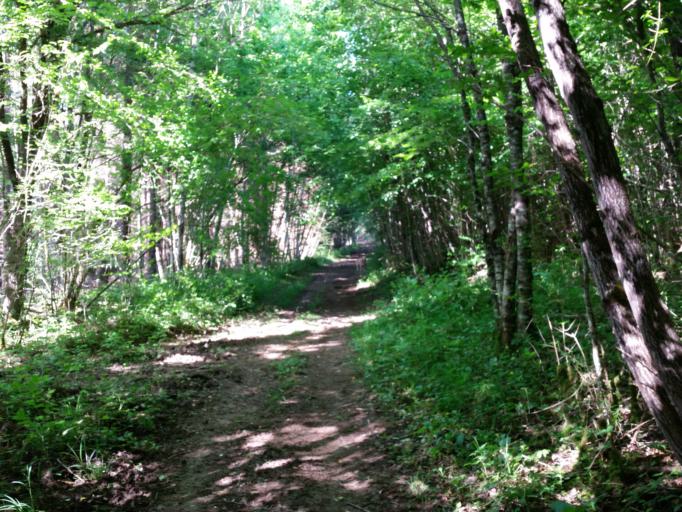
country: FR
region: Franche-Comte
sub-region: Departement du Doubs
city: Quingey
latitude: 47.0381
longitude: 5.9702
